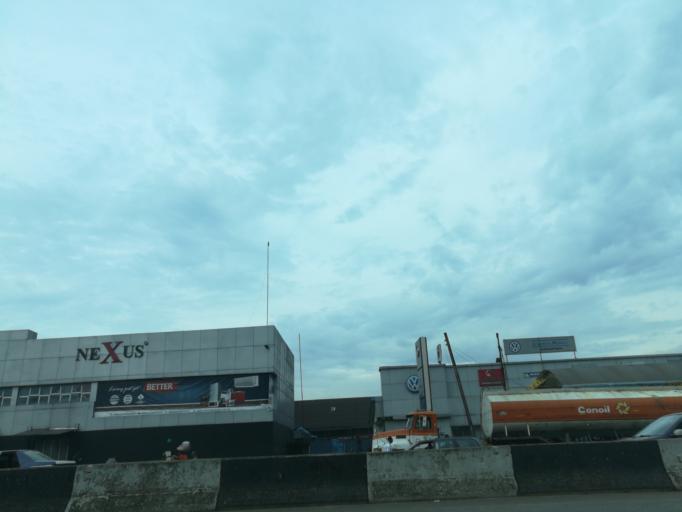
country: NG
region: Rivers
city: Port Harcourt
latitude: 4.7928
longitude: 7.0018
